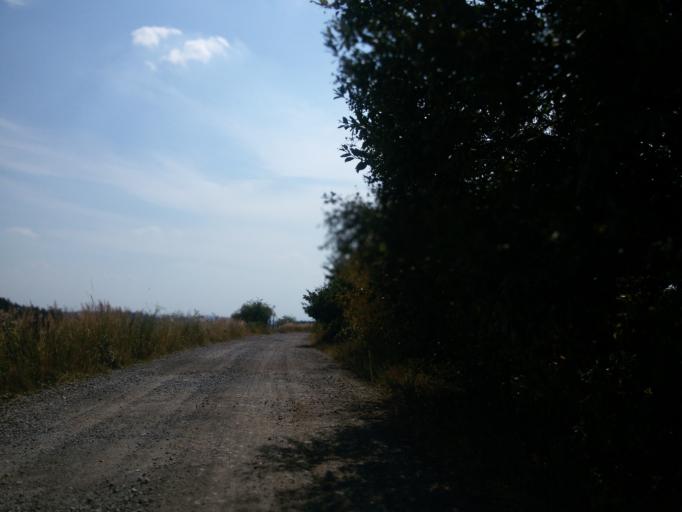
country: CZ
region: South Moravian
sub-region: Okres Brno-Venkov
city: Lomnice
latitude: 49.4375
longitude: 16.4494
